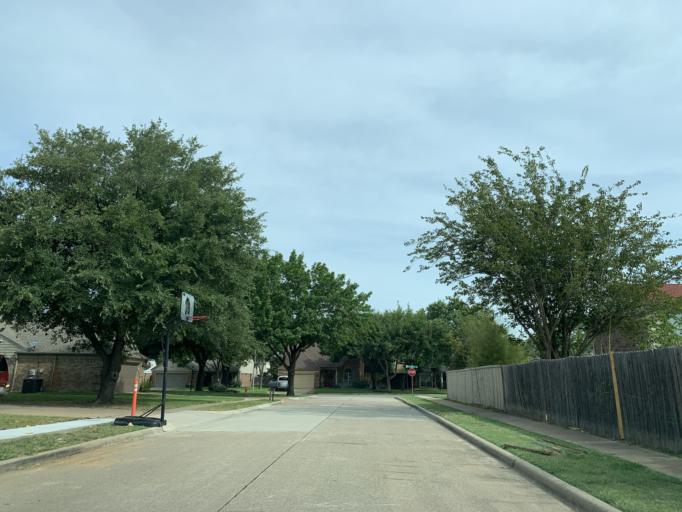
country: US
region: Texas
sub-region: Dallas County
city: Grand Prairie
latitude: 32.6640
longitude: -97.0041
